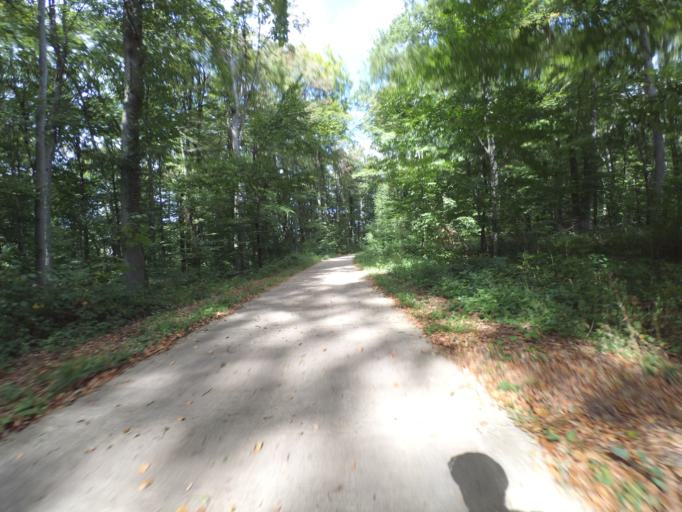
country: LU
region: Grevenmacher
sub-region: Canton de Remich
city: Mondorf-les-Bains
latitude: 49.5224
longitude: 6.3113
